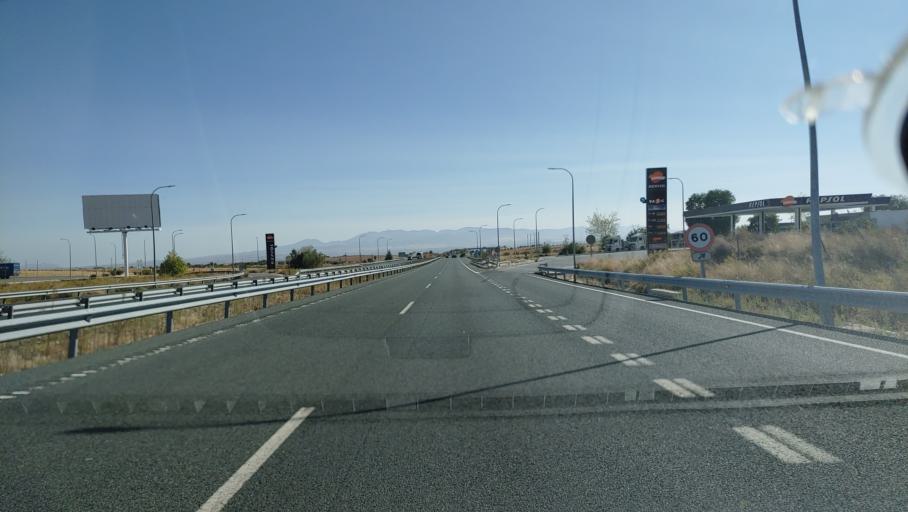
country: ES
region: Andalusia
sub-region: Provincia de Granada
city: Darro
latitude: 37.3208
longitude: -3.2990
